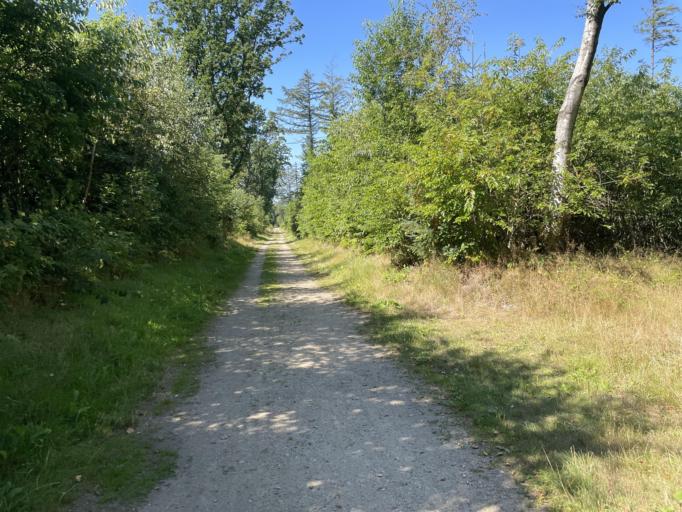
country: DE
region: Schleswig-Holstein
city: Mildstedt
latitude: 54.4713
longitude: 9.1073
